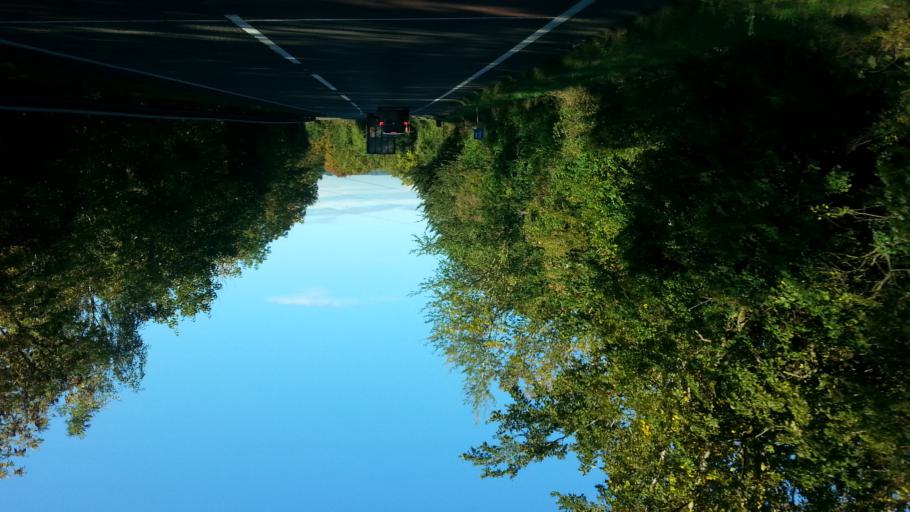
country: GB
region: England
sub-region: Herefordshire
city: Marstow
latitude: 51.8896
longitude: -2.6372
